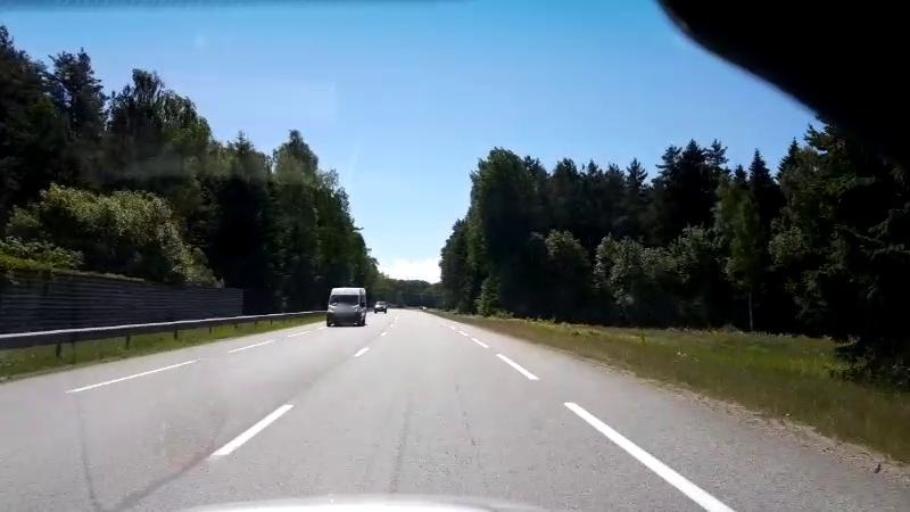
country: LV
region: Saulkrastu
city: Saulkrasti
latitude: 57.4367
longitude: 24.4299
